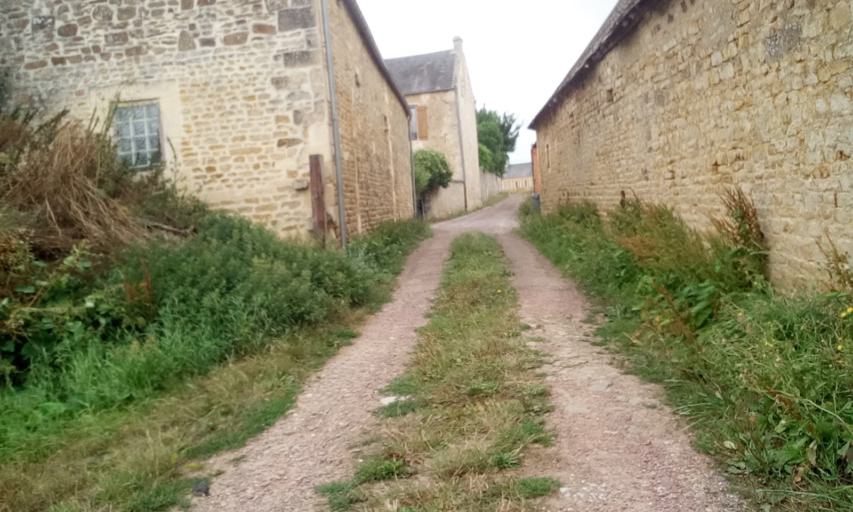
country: FR
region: Lower Normandy
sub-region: Departement du Calvados
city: Tourville-sur-Odon
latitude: 49.1393
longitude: -0.4963
